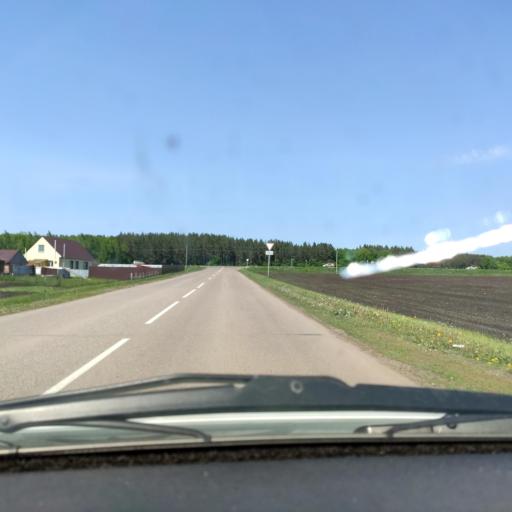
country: RU
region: Bashkortostan
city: Avdon
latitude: 54.5586
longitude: 55.6686
